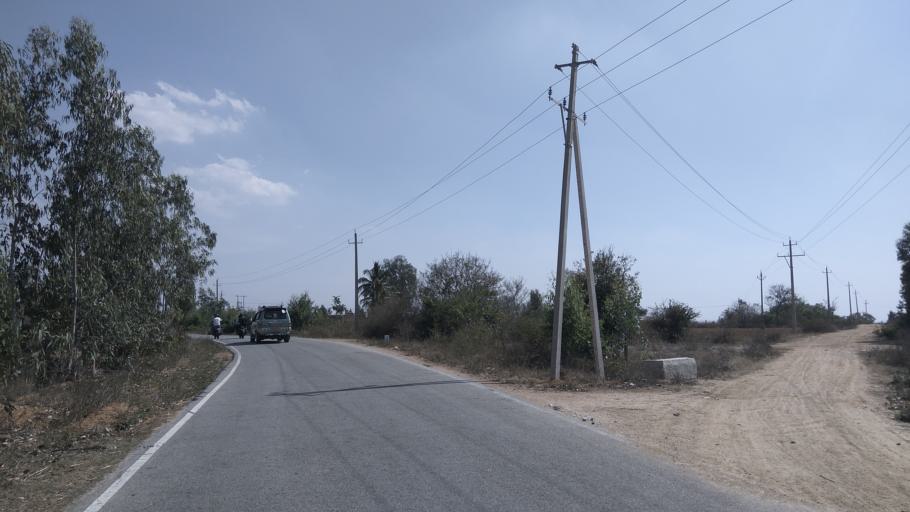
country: IN
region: Karnataka
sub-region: Kolar
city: Mulbagal
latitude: 13.1973
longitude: 78.3548
